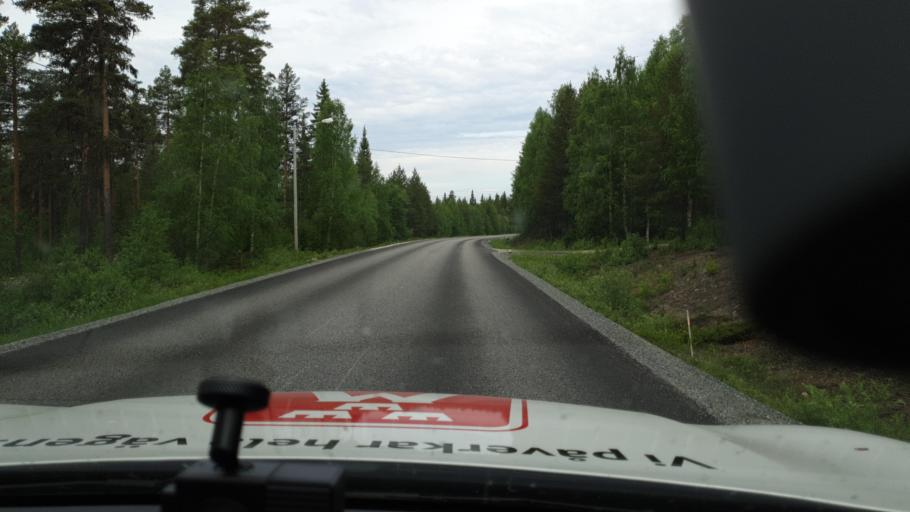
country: SE
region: Vaesterbotten
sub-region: Mala Kommun
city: Mala
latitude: 64.9104
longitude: 18.6653
